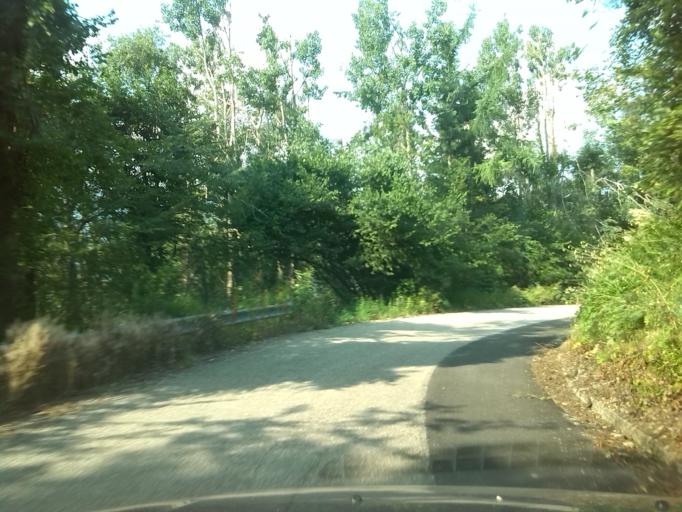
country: IT
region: Friuli Venezia Giulia
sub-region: Provincia di Udine
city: Cras
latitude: 46.1548
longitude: 13.6289
